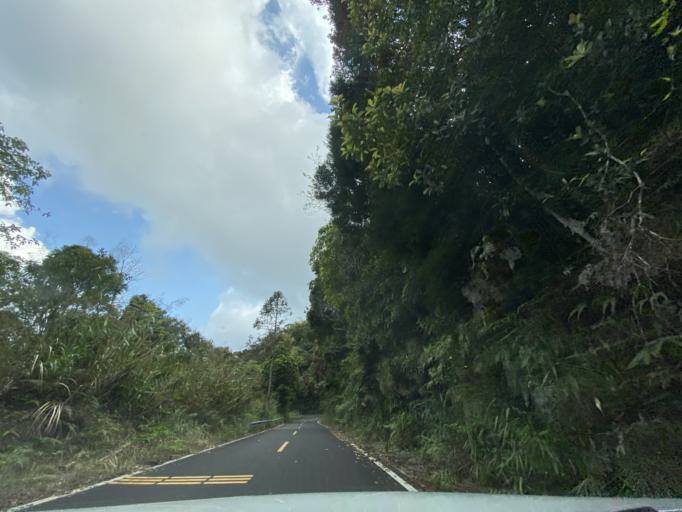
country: CN
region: Hainan
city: Diaoluoshan
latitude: 18.7181
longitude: 109.8787
